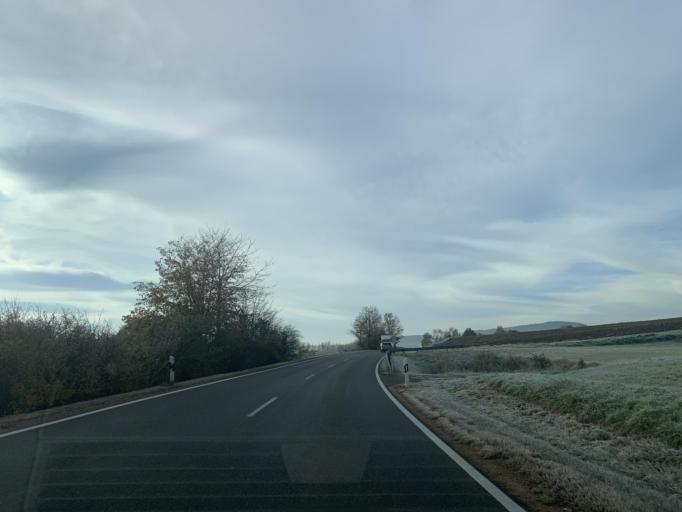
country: DE
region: Bavaria
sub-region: Upper Palatinate
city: Neunburg vorm Wald
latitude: 49.3647
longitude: 12.3787
